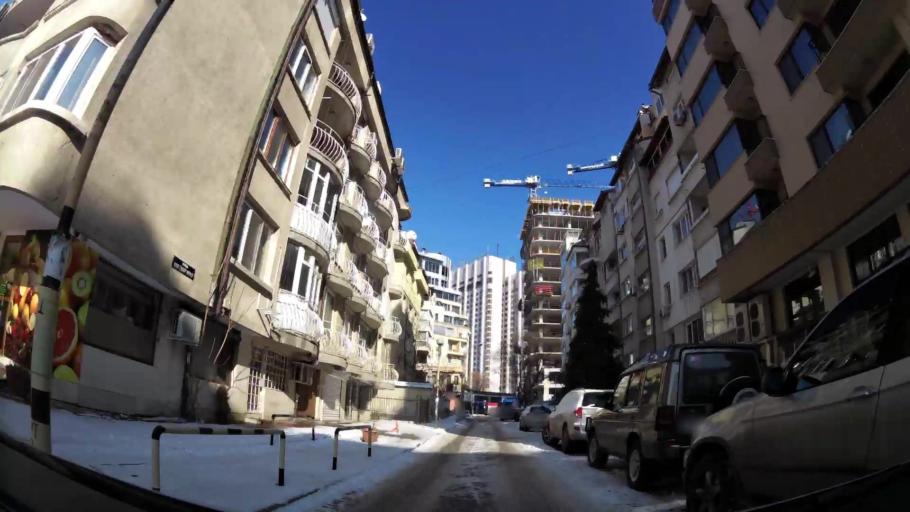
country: BG
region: Sofia-Capital
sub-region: Stolichna Obshtina
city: Sofia
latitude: 42.6703
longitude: 23.3177
